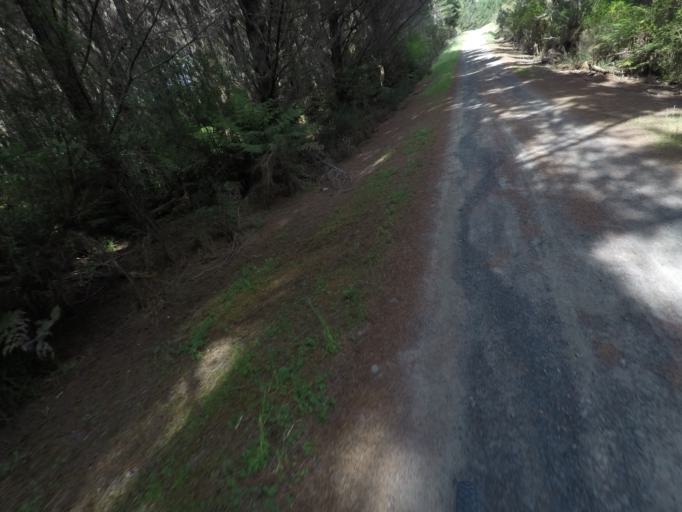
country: NZ
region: Auckland
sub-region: Auckland
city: Muriwai Beach
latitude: -36.7434
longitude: 174.5701
